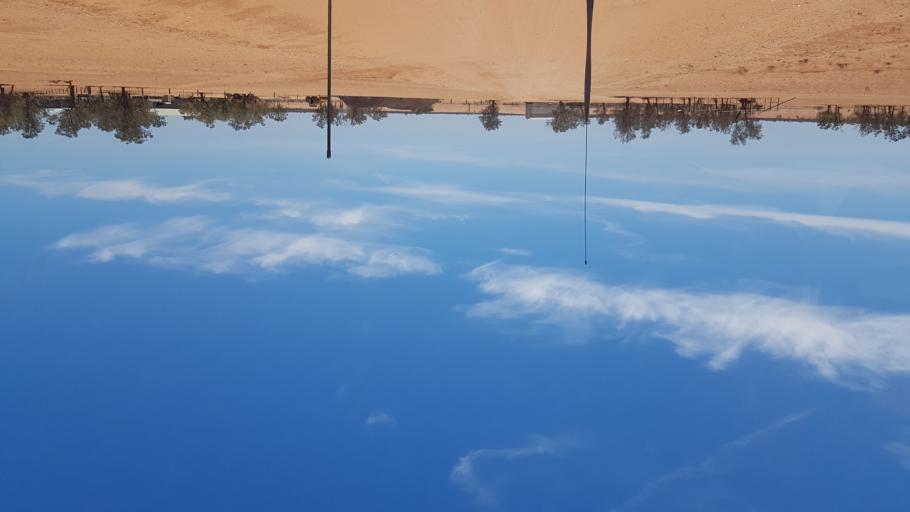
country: AU
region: New South Wales
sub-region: Wentworth
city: Dareton
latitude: -33.3461
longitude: 141.4527
